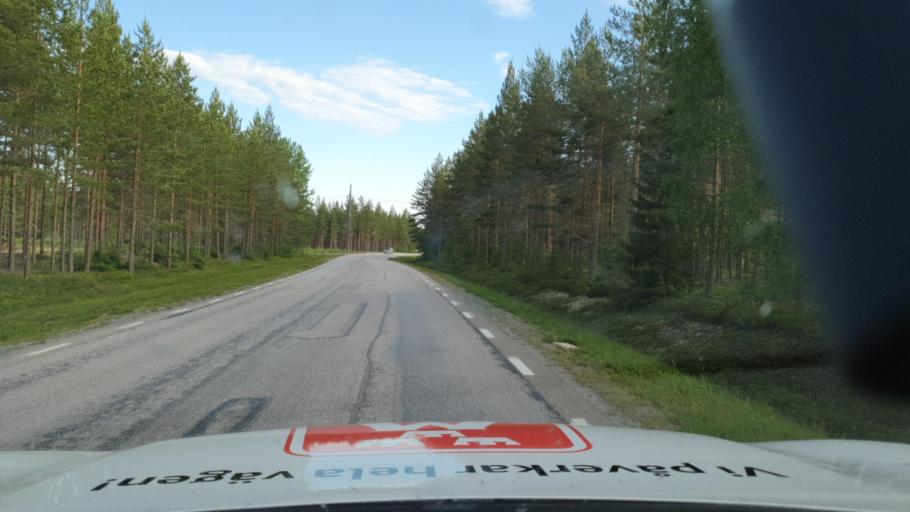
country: SE
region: Vaesterbotten
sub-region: Umea Kommun
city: Roback
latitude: 63.8633
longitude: 20.1444
